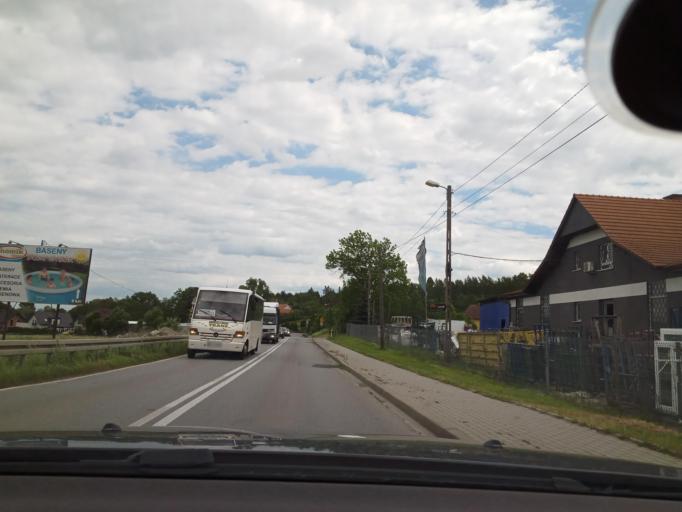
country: PL
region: Lesser Poland Voivodeship
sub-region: Powiat wielicki
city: Trabki
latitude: 49.9556
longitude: 20.1512
